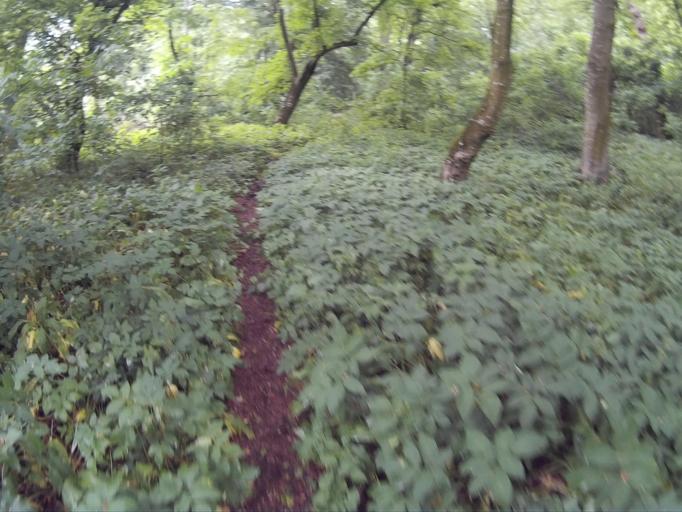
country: HU
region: Veszprem
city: Sumeg
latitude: 46.9080
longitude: 17.2584
